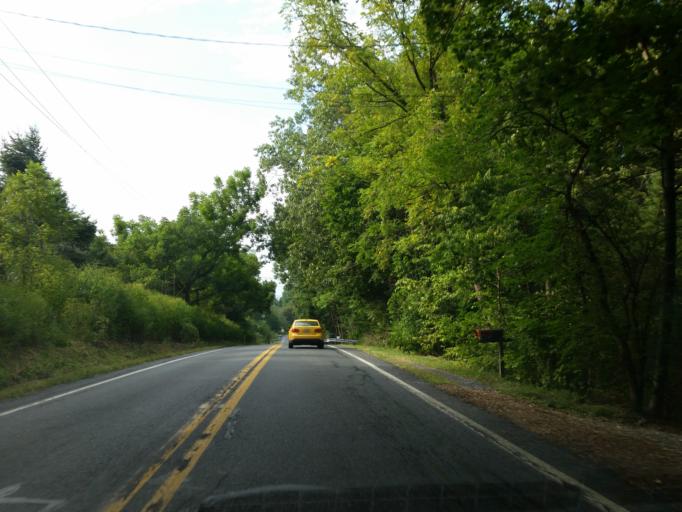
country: US
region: Pennsylvania
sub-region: Lebanon County
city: Annville
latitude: 40.3509
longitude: -76.5266
